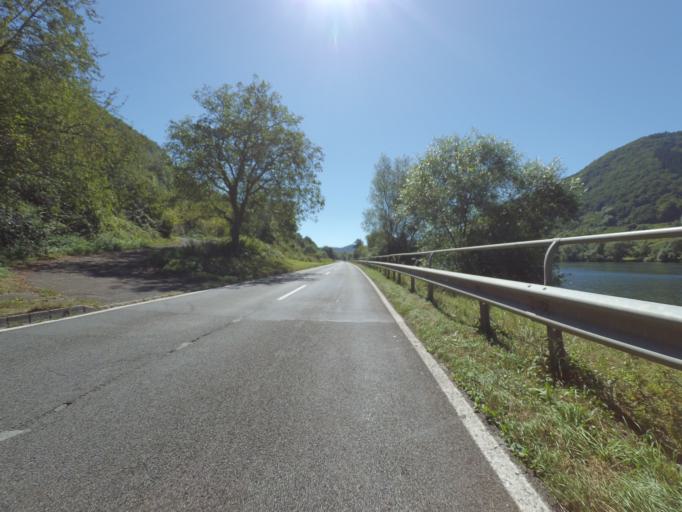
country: DE
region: Rheinland-Pfalz
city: Bullay
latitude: 50.0700
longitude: 7.1325
